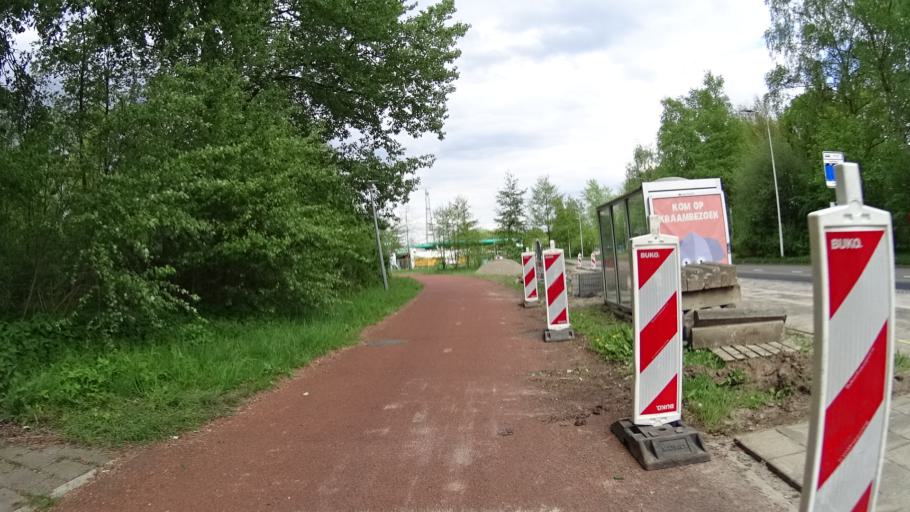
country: NL
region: North Brabant
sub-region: Gemeente Eindhoven
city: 't Hofke
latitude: 51.4540
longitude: 5.5203
